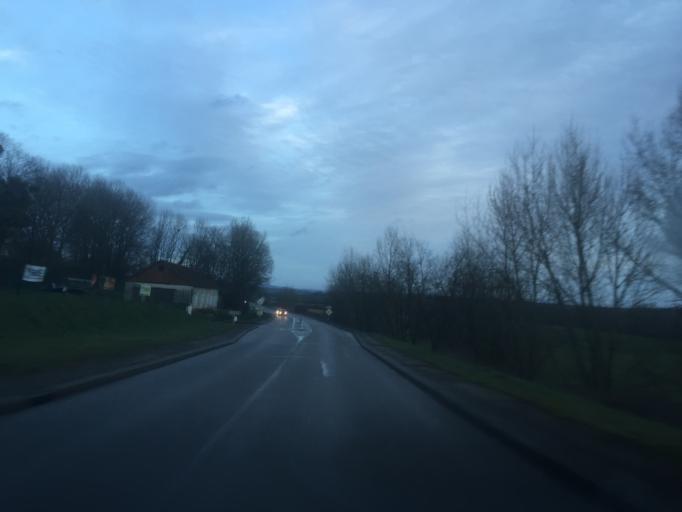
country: FR
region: Franche-Comte
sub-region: Departement du Jura
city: Orchamps
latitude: 47.1456
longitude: 5.6661
